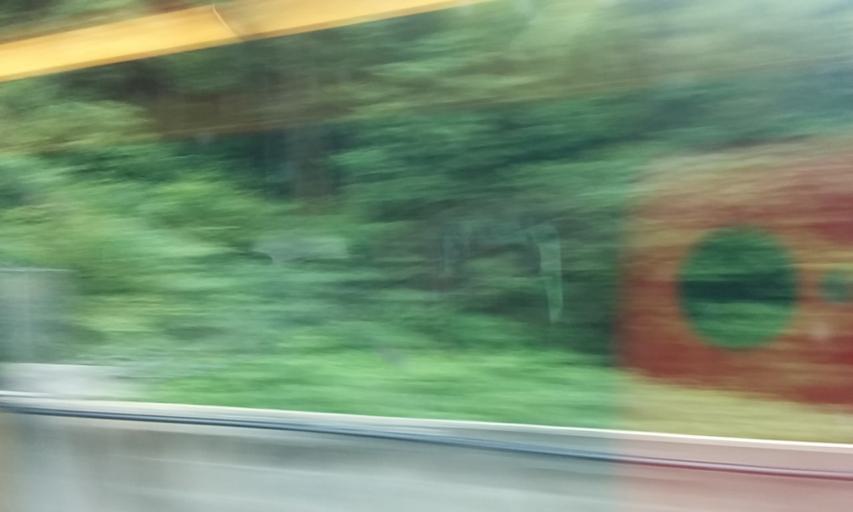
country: JP
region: Tochigi
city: Kuroiso
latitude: 37.0903
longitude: 140.1579
